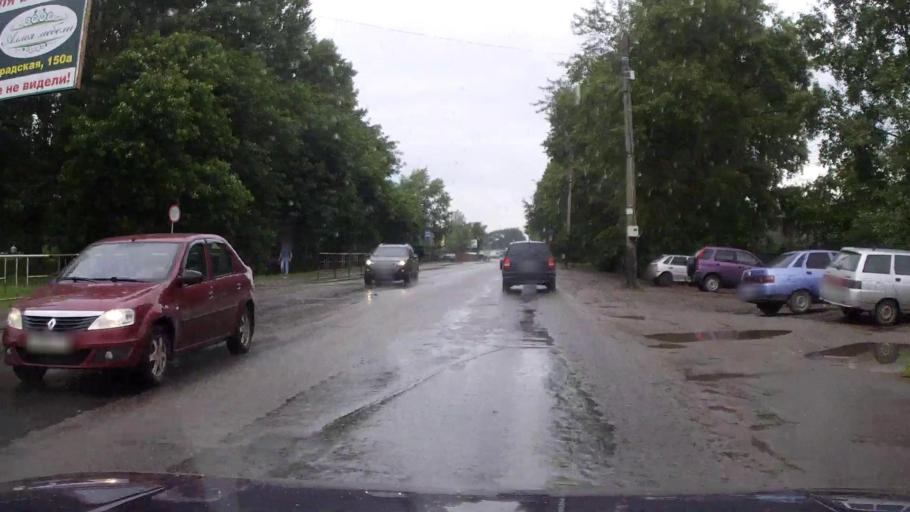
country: RU
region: Vologda
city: Vologda
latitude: 59.2091
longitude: 39.8580
